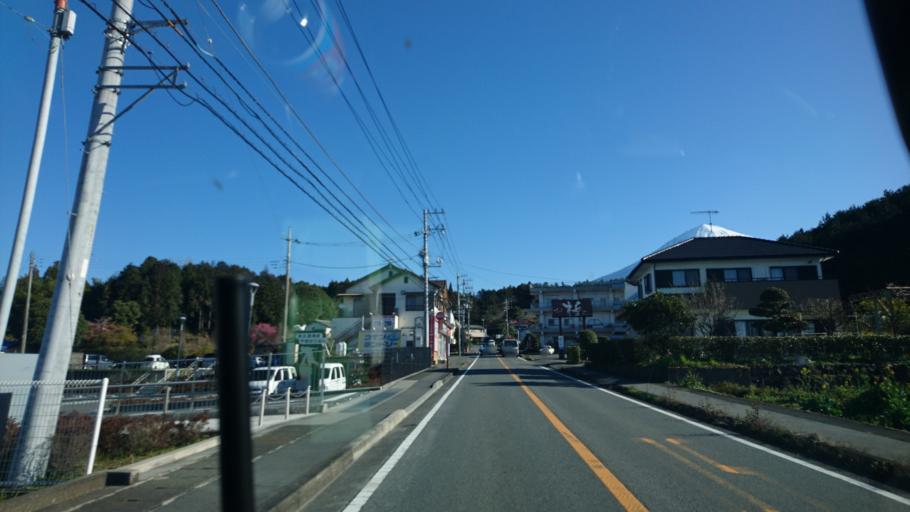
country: JP
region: Shizuoka
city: Fujinomiya
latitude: 35.2675
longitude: 138.6040
